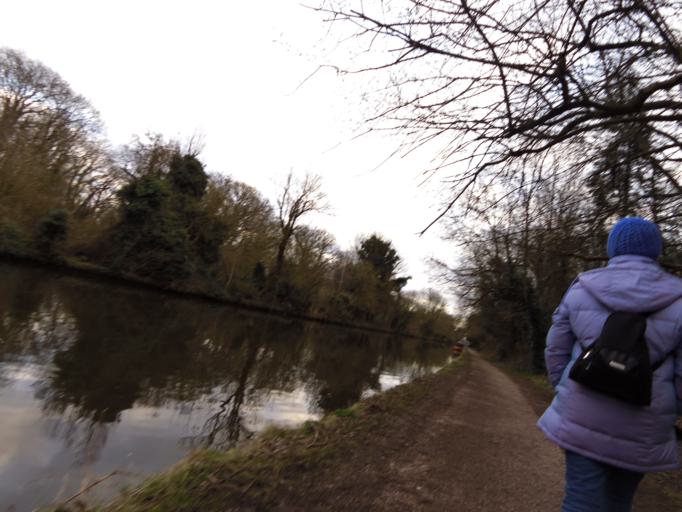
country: GB
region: England
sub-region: Hertfordshire
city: Watford
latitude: 51.6593
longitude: -0.4277
